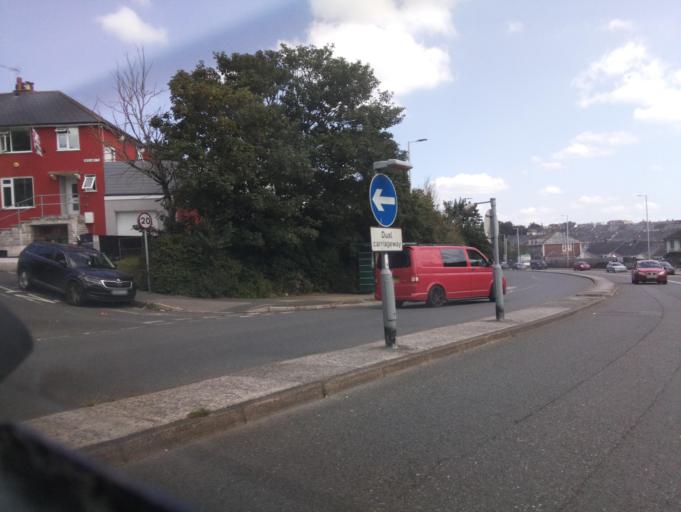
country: GB
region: England
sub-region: Plymouth
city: Plymouth
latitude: 50.3876
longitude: -4.1643
